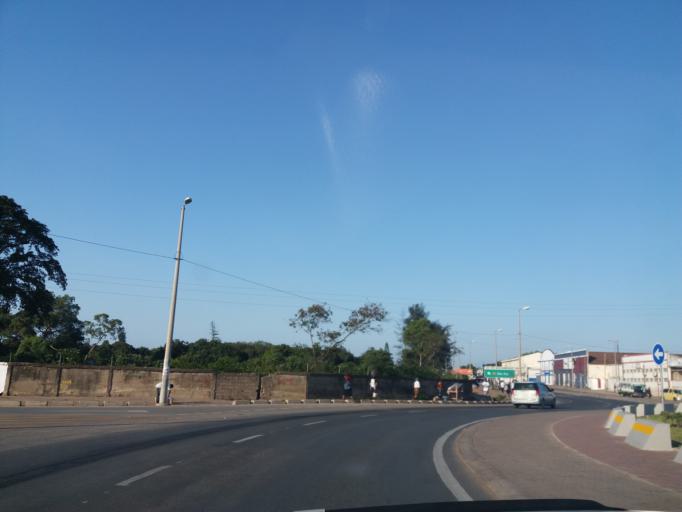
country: MZ
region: Maputo City
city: Maputo
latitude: -25.9344
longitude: 32.5502
